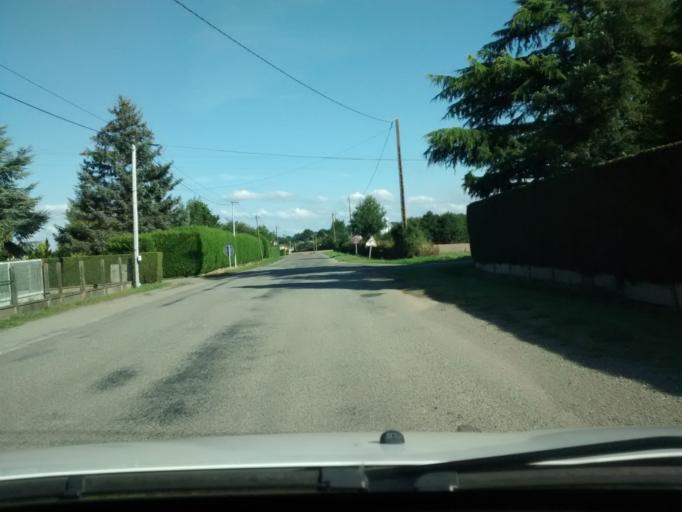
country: FR
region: Brittany
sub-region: Departement d'Ille-et-Vilaine
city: Nouvoitou
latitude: 48.0717
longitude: -1.5687
